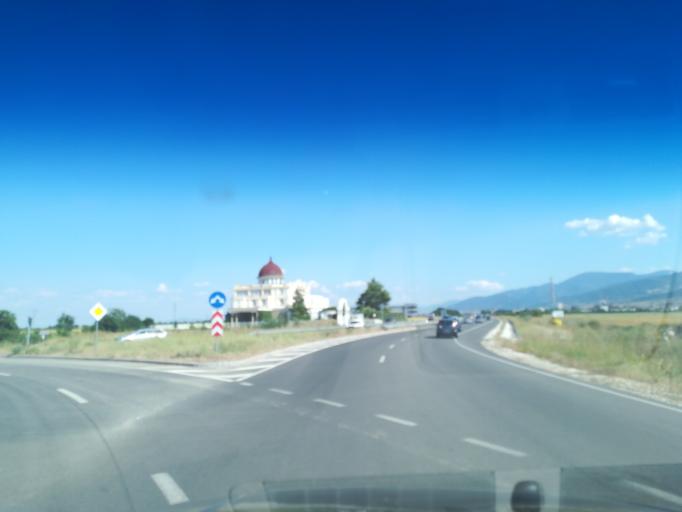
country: BG
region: Plovdiv
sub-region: Obshtina Plovdiv
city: Plovdiv
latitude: 42.0800
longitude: 24.8014
